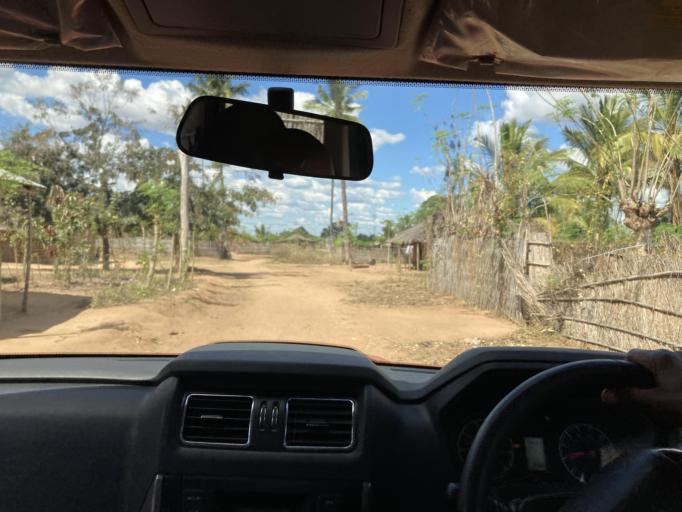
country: MZ
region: Cabo Delgado
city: Montepuez
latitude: -13.1461
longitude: 38.9969
